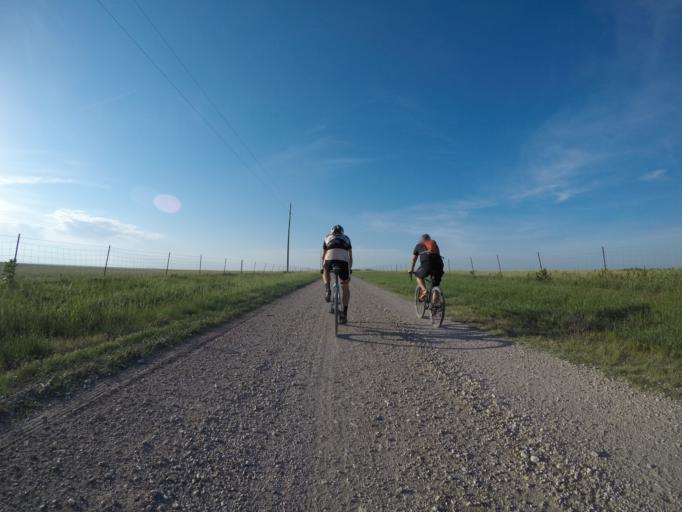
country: US
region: Kansas
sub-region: Riley County
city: Manhattan
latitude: 39.0078
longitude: -96.4920
